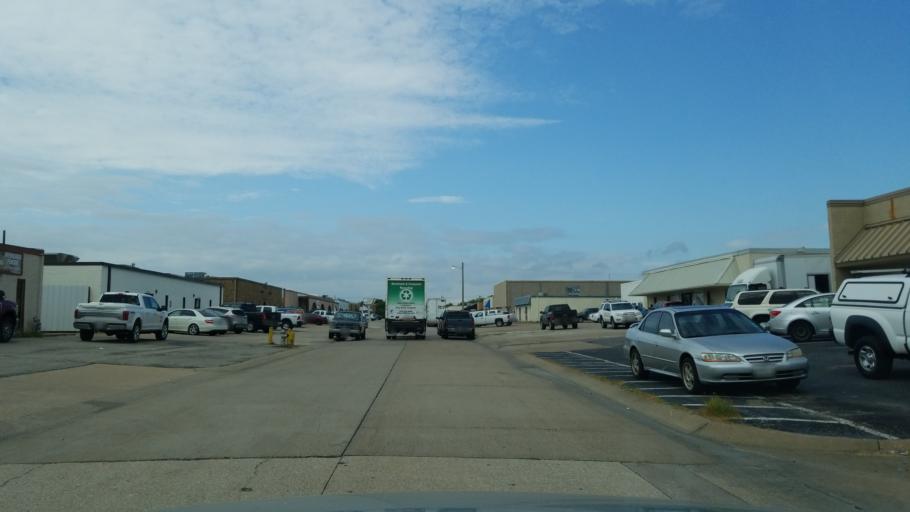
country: US
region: Texas
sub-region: Dallas County
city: Garland
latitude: 32.8988
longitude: -96.6879
